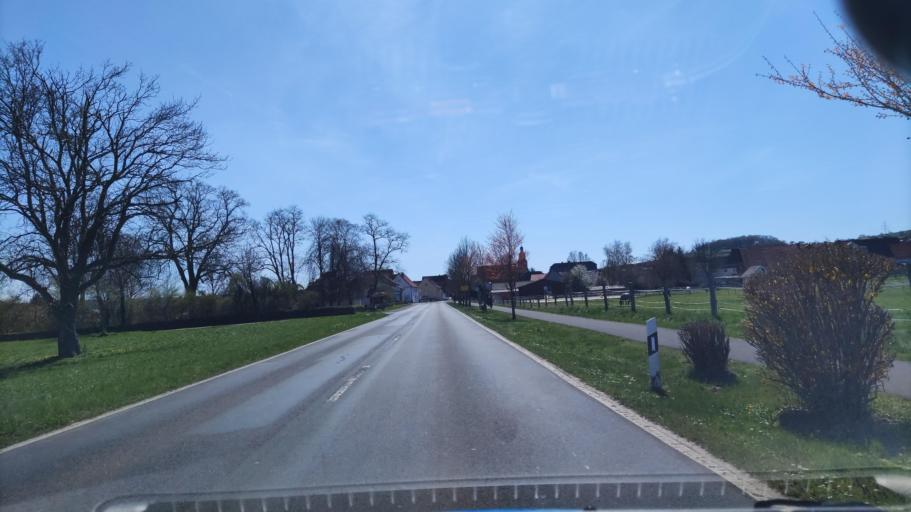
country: DE
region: Hesse
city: Trendelburg
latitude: 51.5965
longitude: 9.4091
